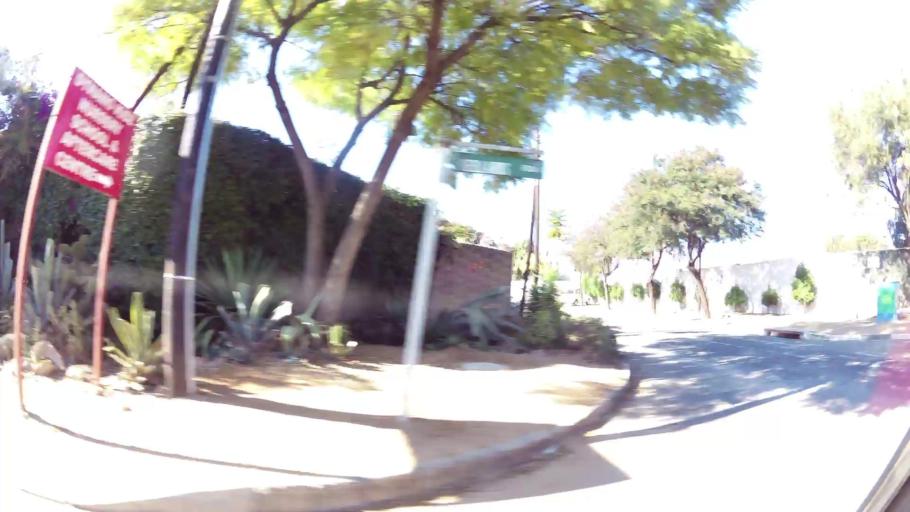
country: ZA
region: Gauteng
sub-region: West Rand District Municipality
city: Muldersdriseloop
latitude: -26.0537
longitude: 27.9659
